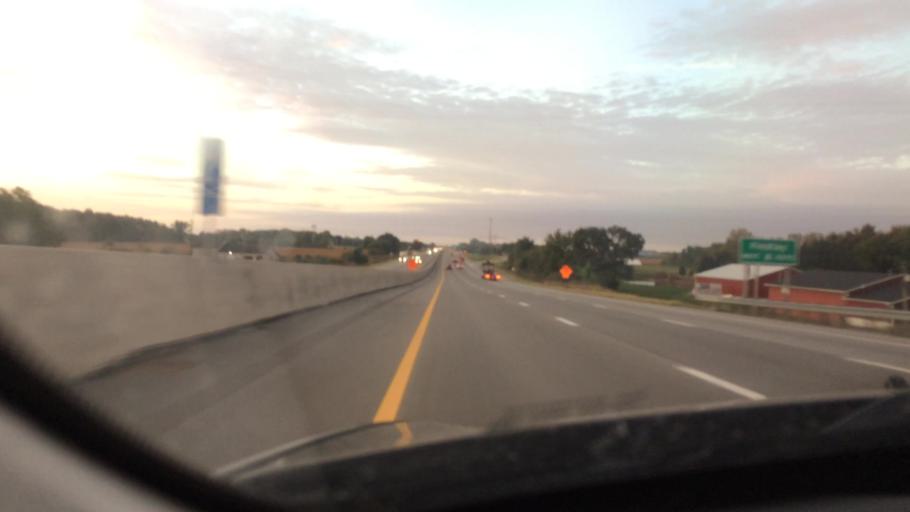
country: US
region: Ohio
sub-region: Hancock County
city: Findlay
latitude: 41.1083
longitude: -83.6599
